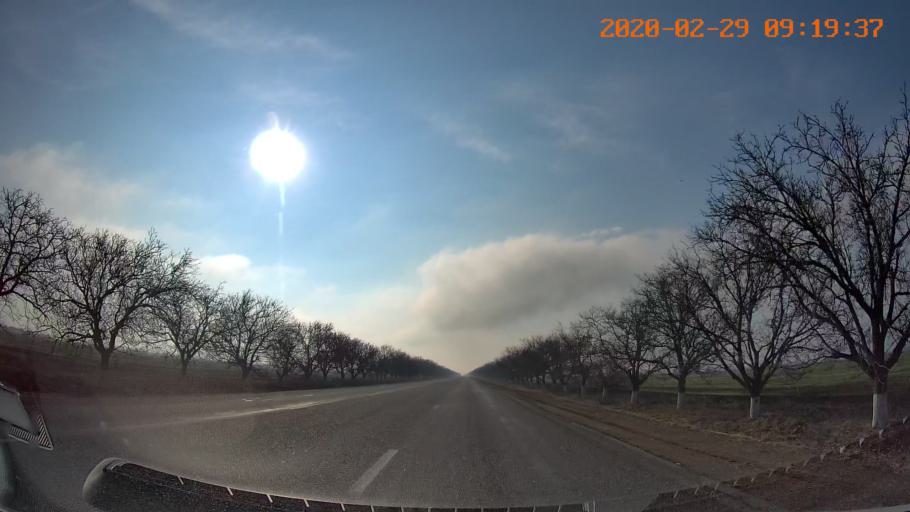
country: MD
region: Telenesti
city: Pervomaisc
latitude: 46.7604
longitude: 29.9407
